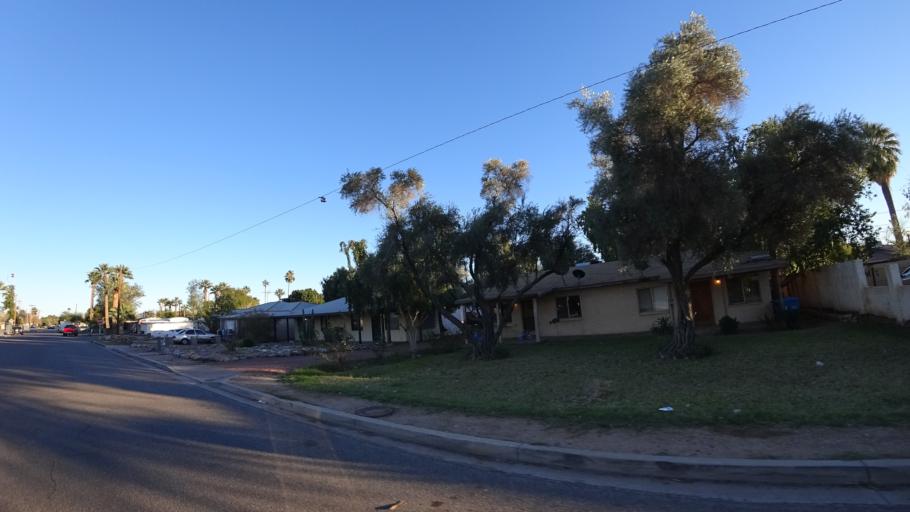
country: US
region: Arizona
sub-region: Maricopa County
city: Phoenix
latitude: 33.4767
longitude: -112.0158
